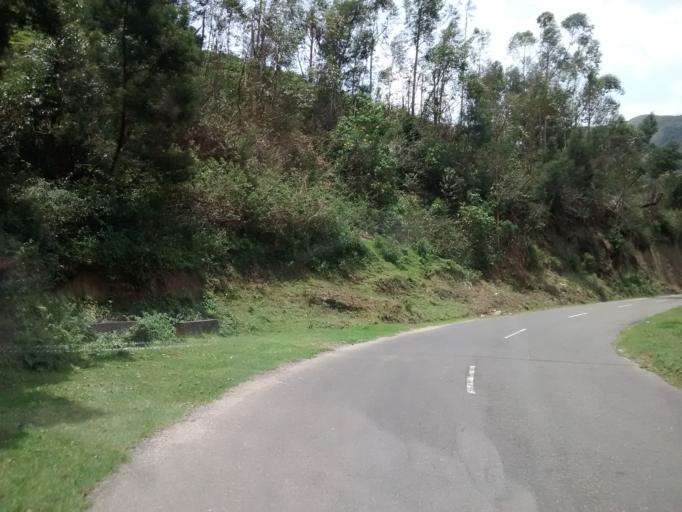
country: IN
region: Kerala
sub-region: Idukki
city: Munnar
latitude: 10.1320
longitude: 77.2046
